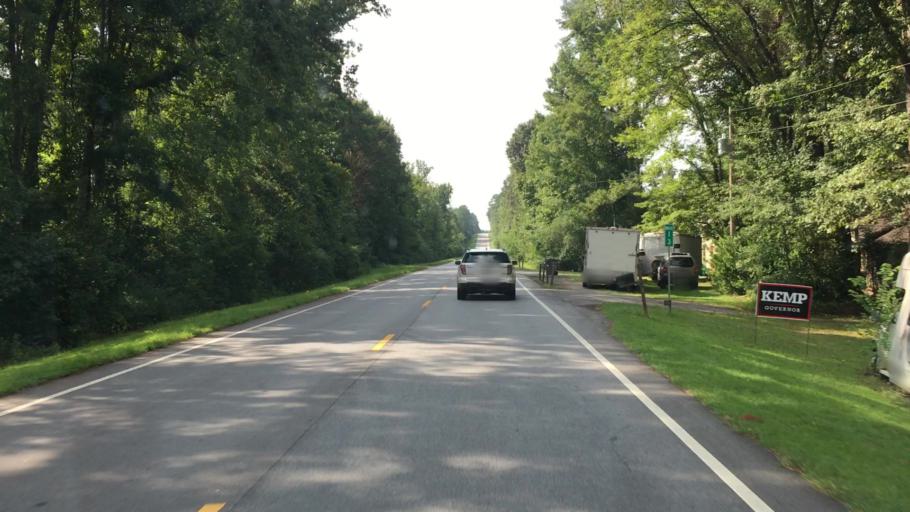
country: US
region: Georgia
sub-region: Jasper County
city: Monticello
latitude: 33.3191
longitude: -83.6957
